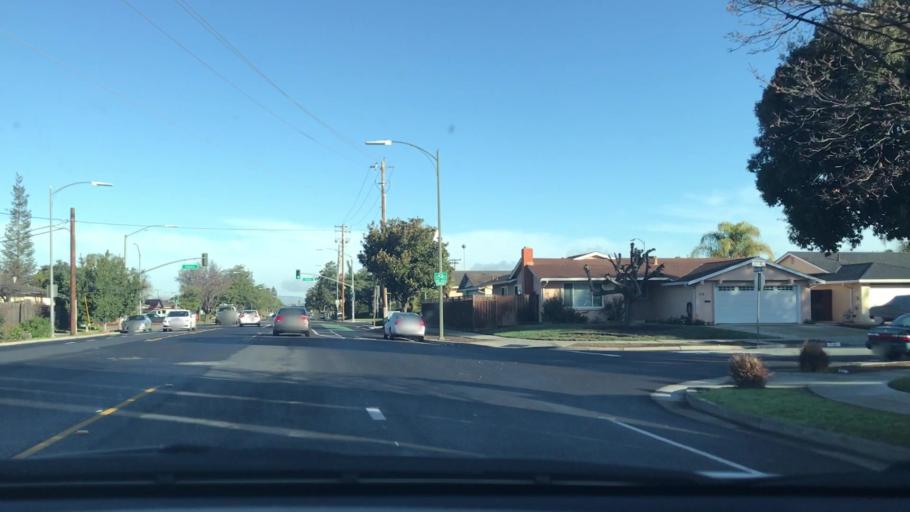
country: US
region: California
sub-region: Santa Clara County
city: Seven Trees
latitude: 37.2412
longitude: -121.8397
